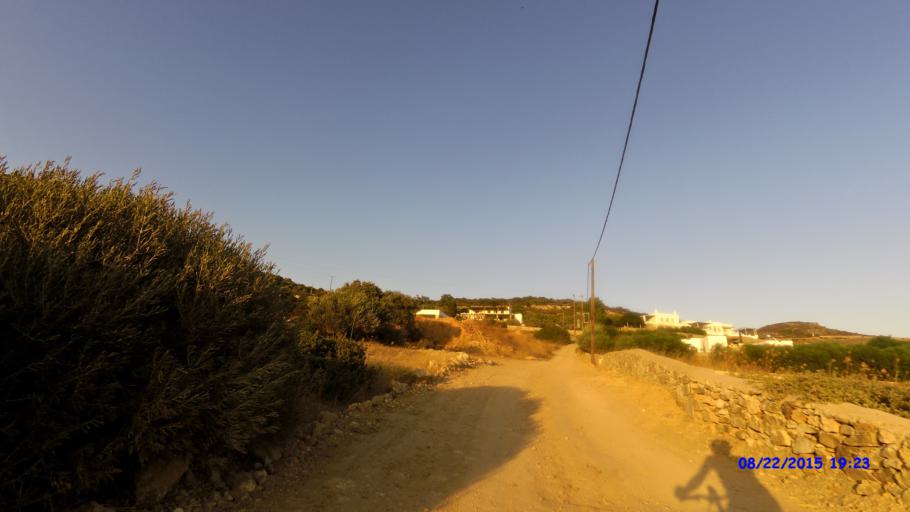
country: GR
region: South Aegean
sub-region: Nomos Kykladon
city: Antiparos
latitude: 36.9729
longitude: 25.0442
